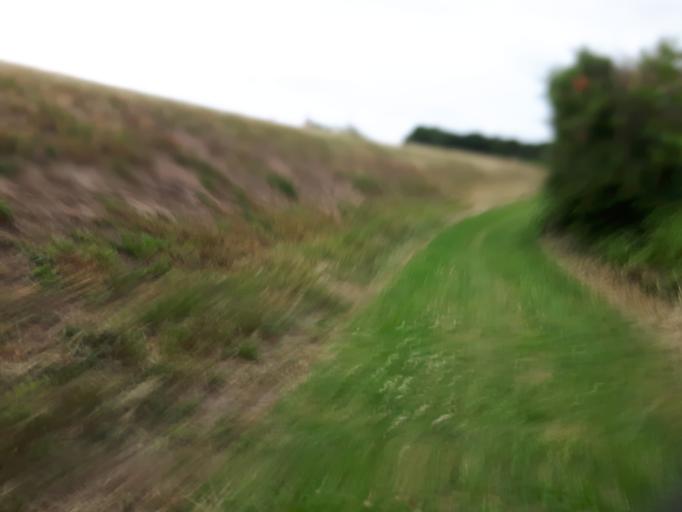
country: DE
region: Lower Saxony
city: Winsen
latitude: 53.3722
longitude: 10.2000
